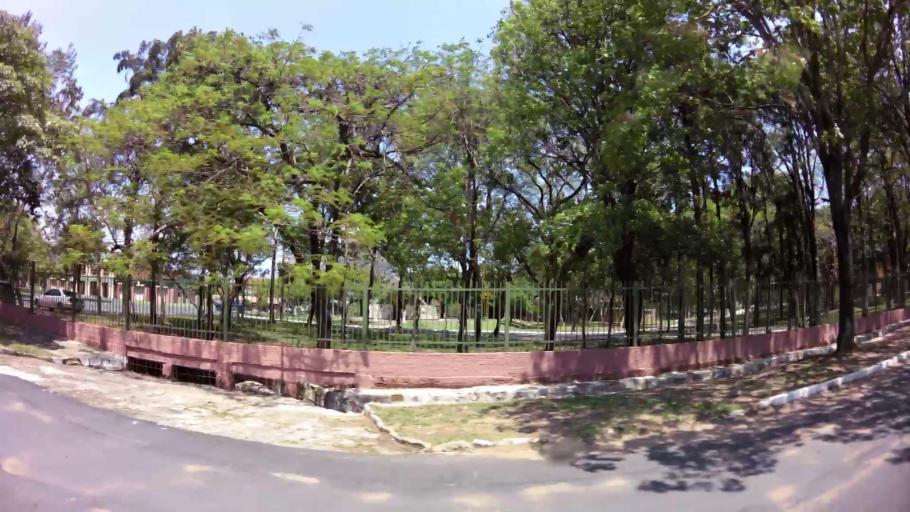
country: PY
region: Asuncion
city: Asuncion
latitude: -25.3044
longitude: -57.6535
